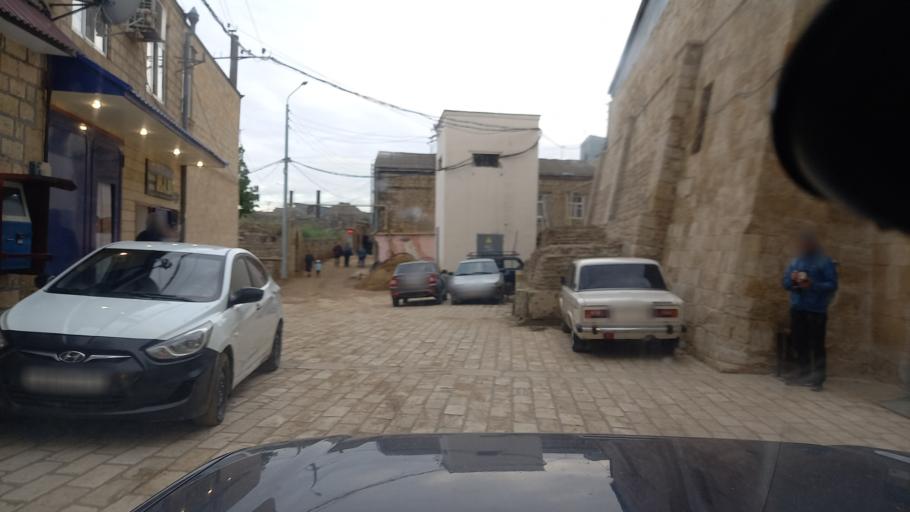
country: RU
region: Dagestan
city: Derbent
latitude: 42.0555
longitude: 48.2802
